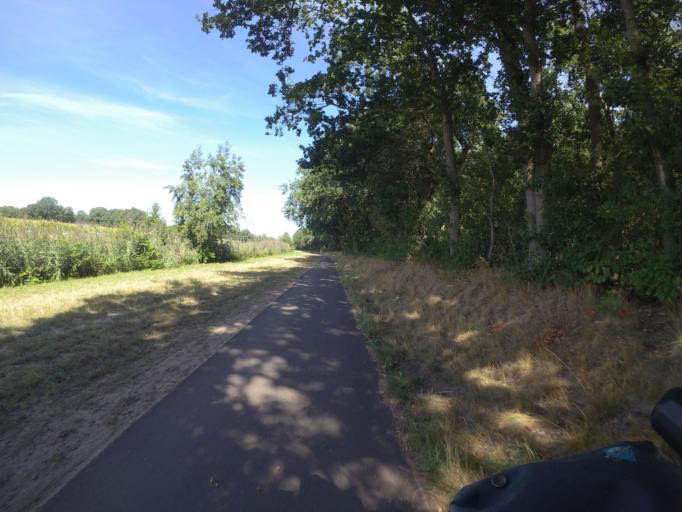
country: NL
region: Overijssel
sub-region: Gemeente Twenterand
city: Den Ham
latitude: 52.4092
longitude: 6.4052
